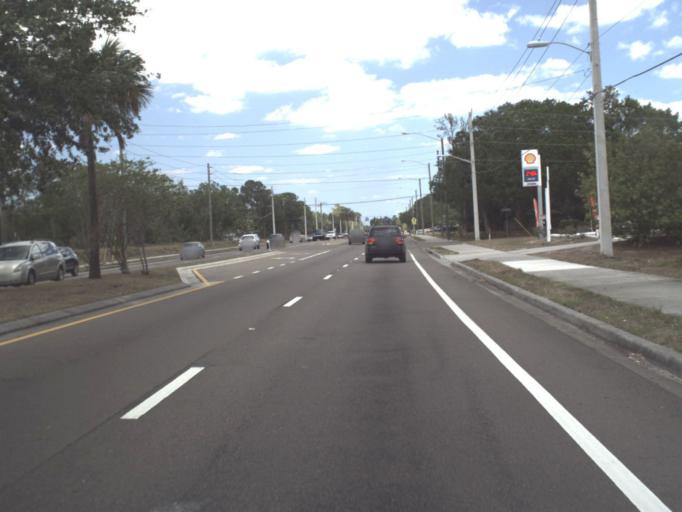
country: US
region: Florida
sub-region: Brevard County
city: Palm Bay
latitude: 28.0013
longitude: -80.6218
